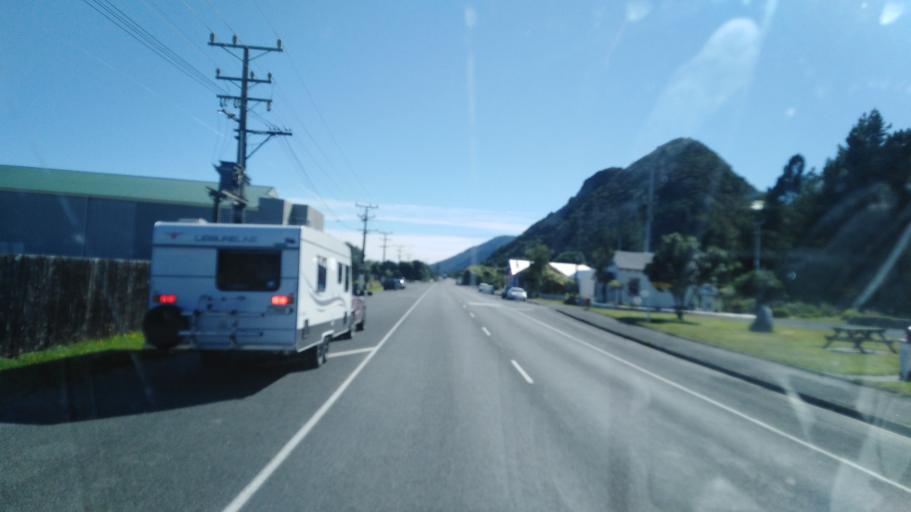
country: NZ
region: West Coast
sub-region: Buller District
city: Westport
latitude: -41.6292
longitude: 171.8544
